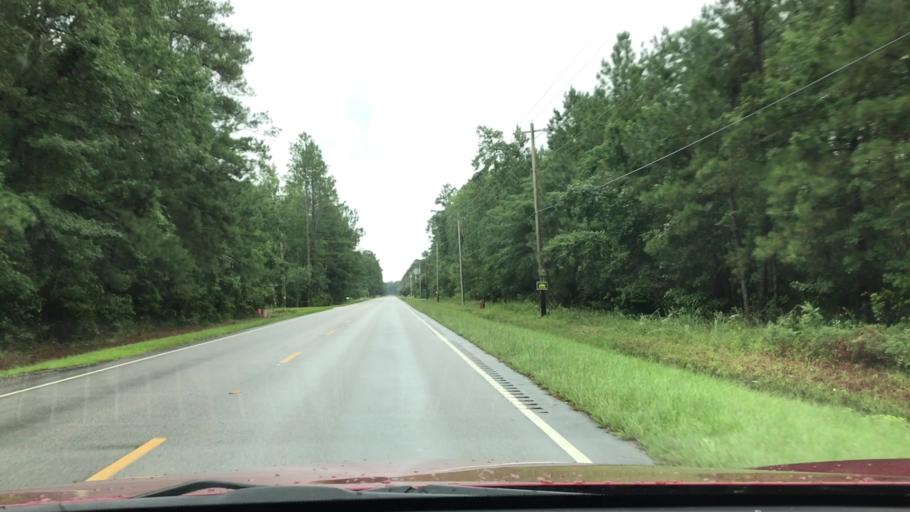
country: US
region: South Carolina
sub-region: Horry County
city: Conway
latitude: 33.7843
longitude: -79.0750
